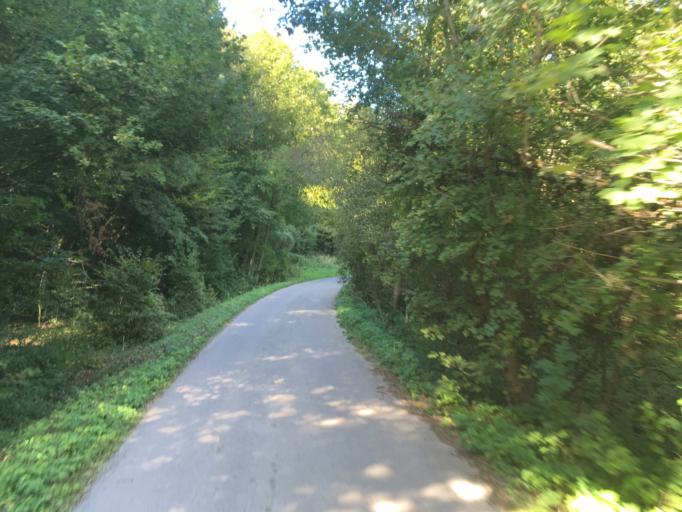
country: SK
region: Trenciansky
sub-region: Okres Povazska Bystrica
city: Povazska Bystrica
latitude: 49.0290
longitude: 18.4350
